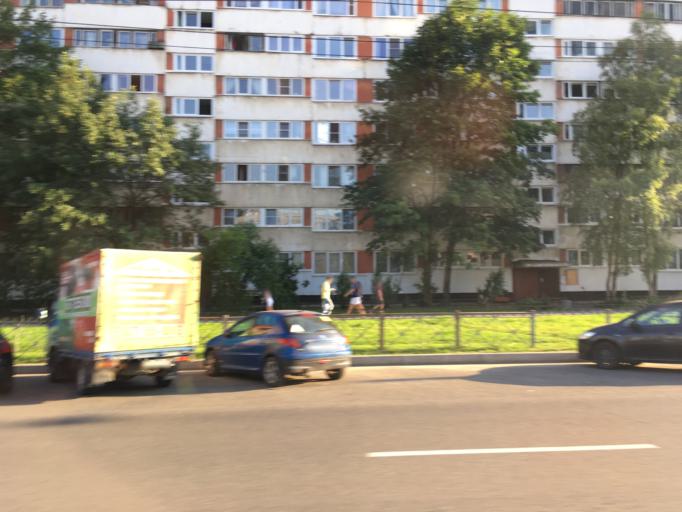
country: RU
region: St.-Petersburg
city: Kolomyagi
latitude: 60.0096
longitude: 30.2922
